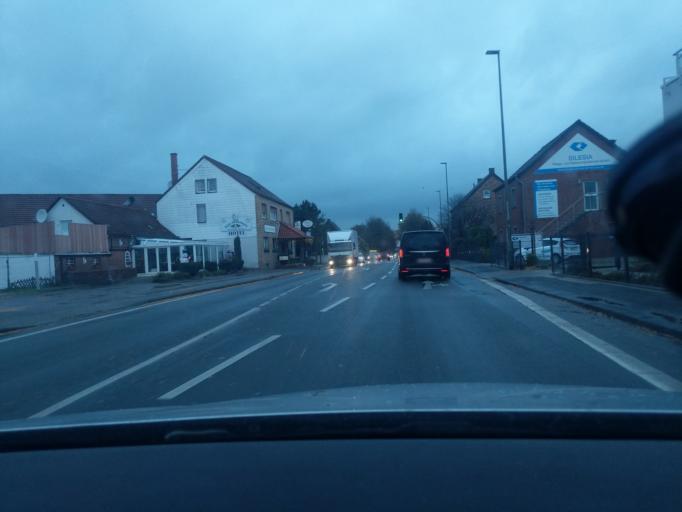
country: DE
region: North Rhine-Westphalia
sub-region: Regierungsbezirk Arnsberg
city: Hamm
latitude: 51.6489
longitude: 7.8415
